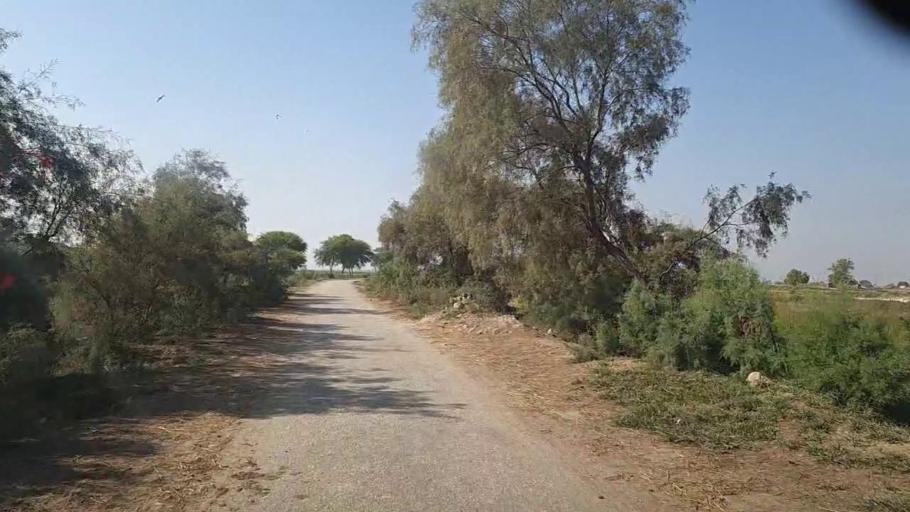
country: PK
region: Sindh
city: Tangwani
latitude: 28.2500
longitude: 68.9418
